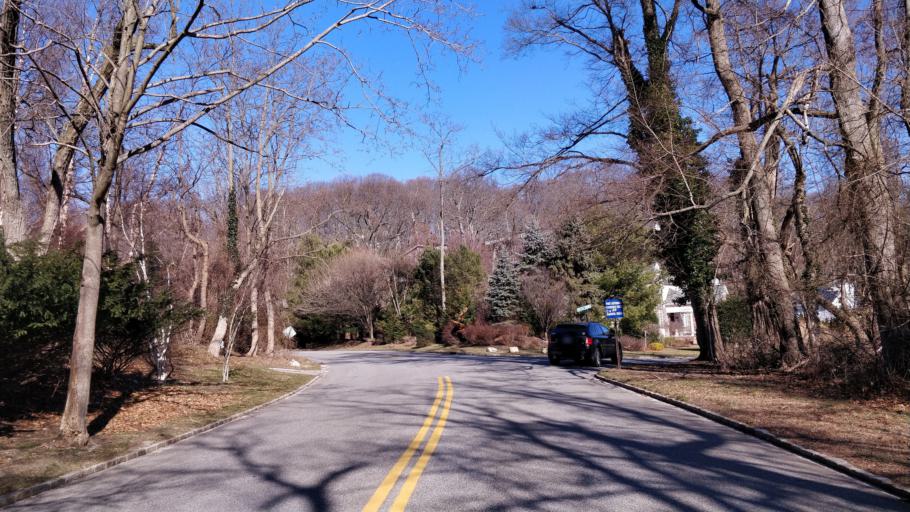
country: US
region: New York
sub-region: Suffolk County
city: Mount Sinai
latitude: 40.9569
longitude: -73.0455
